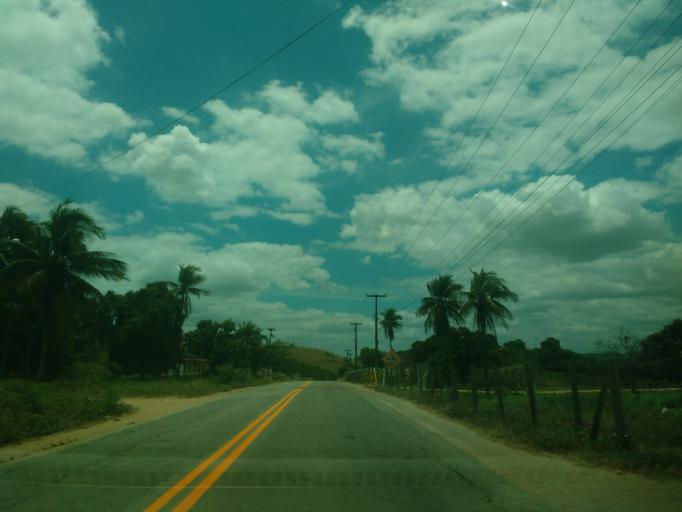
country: BR
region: Alagoas
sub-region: Uniao Dos Palmares
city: Uniao dos Palmares
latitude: -9.1421
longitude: -36.0485
